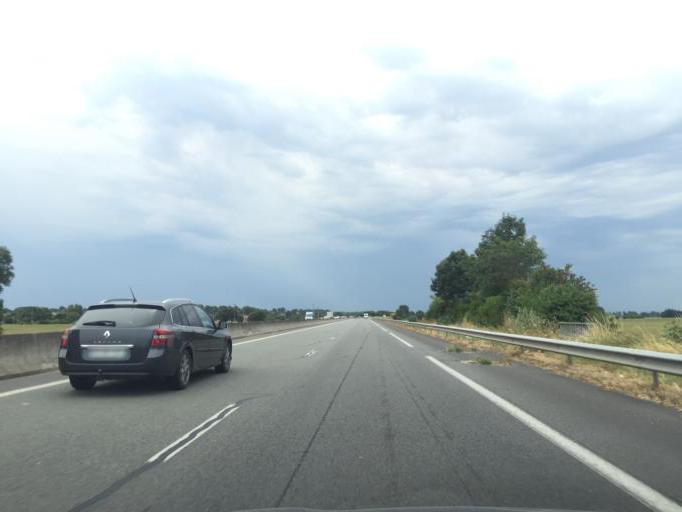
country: FR
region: Auvergne
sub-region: Departement de l'Allier
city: Toulon-sur-Allier
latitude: 46.5188
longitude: 3.3525
